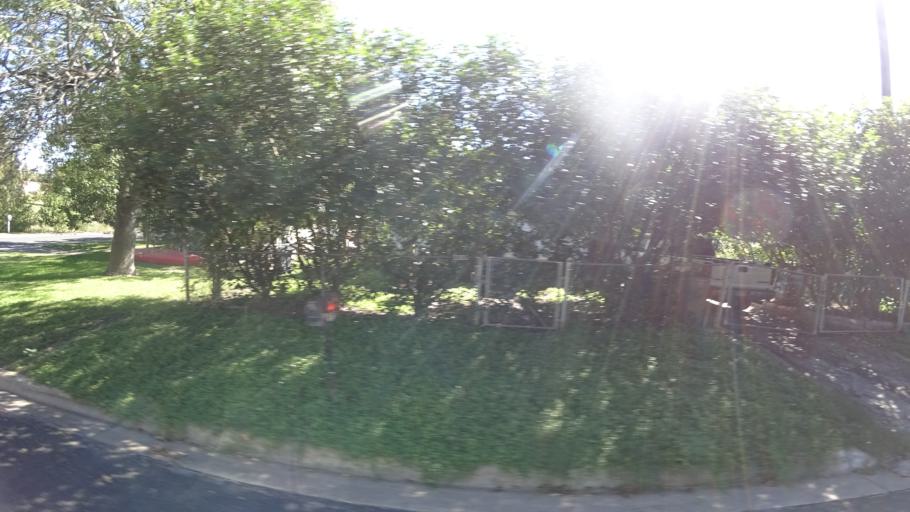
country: US
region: Texas
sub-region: Travis County
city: Austin
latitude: 30.2857
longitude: -97.7017
